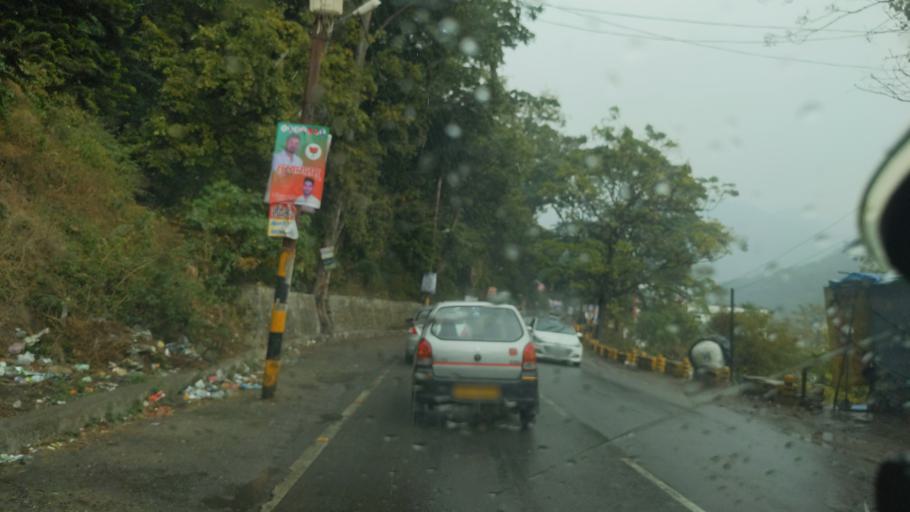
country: IN
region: Uttarakhand
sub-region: Naini Tal
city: Haldwani
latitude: 29.2827
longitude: 79.5451
